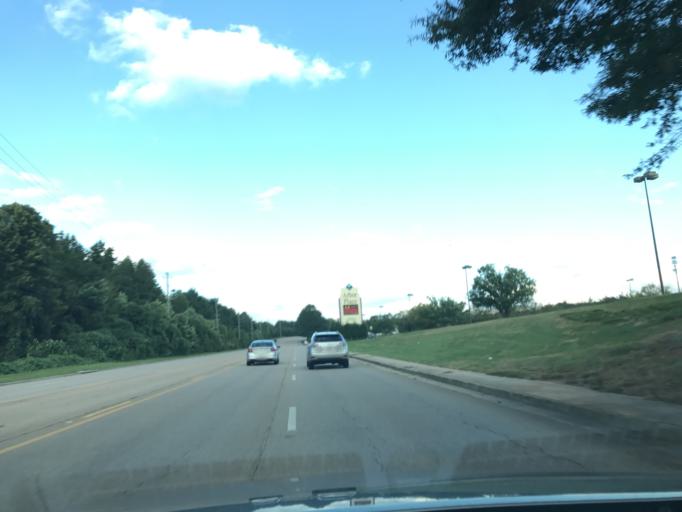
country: US
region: Georgia
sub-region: Douglas County
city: Douglasville
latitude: 33.7297
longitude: -84.7477
